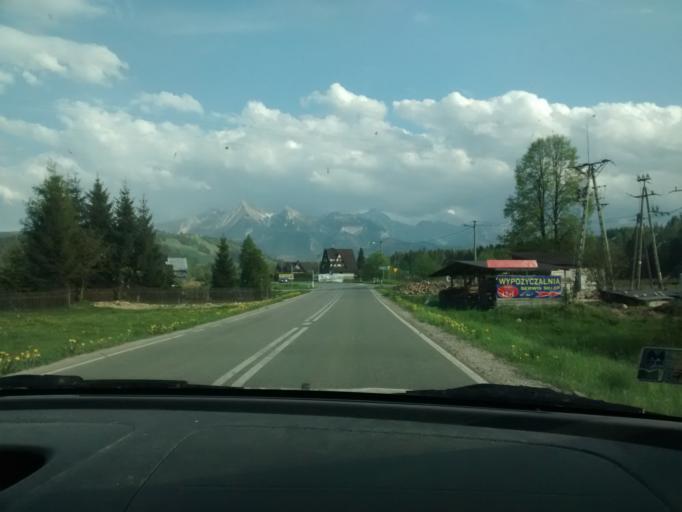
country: PL
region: Lesser Poland Voivodeship
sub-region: Powiat tatrzanski
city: Bukowina Tatrzanska
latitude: 49.3348
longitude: 20.1464
